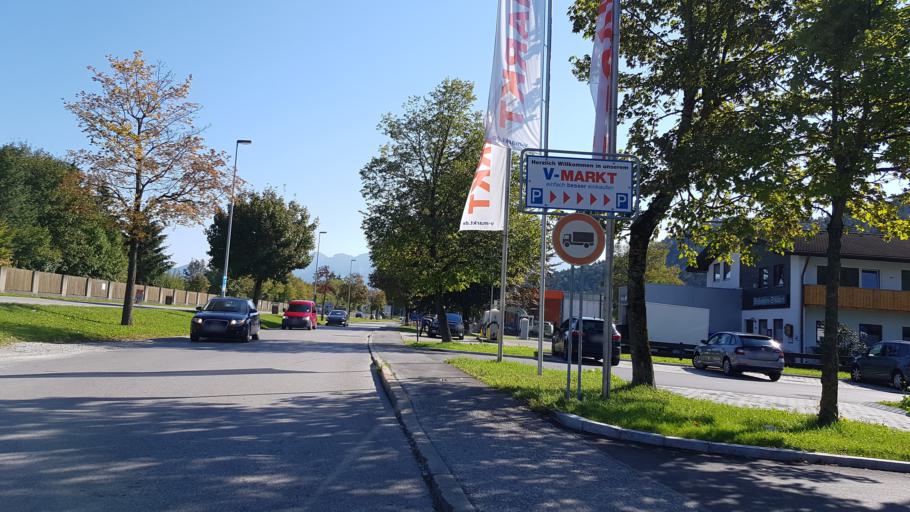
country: DE
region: Bavaria
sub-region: Swabia
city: Fuessen
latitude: 47.5689
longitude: 10.6696
